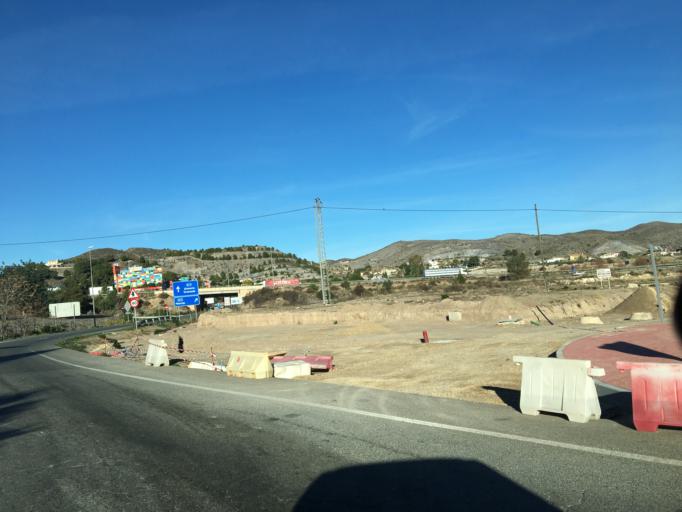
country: ES
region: Murcia
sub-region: Murcia
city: Puerto Lumbreras
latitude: 37.5743
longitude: -1.7965
